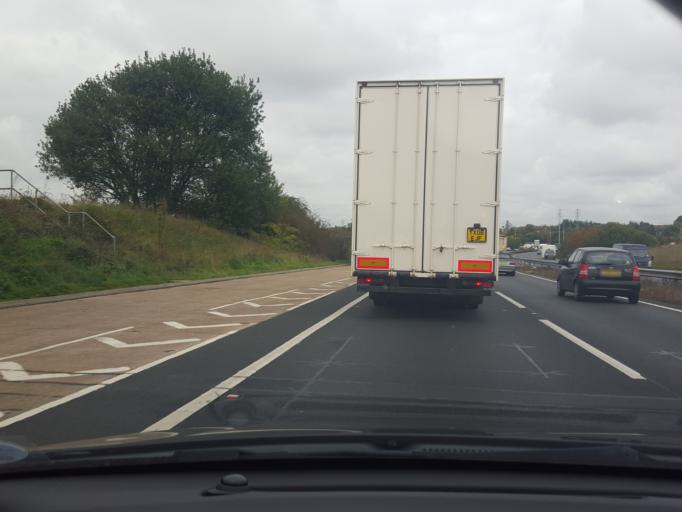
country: GB
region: England
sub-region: Suffolk
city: Bramford
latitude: 52.0320
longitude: 1.0955
